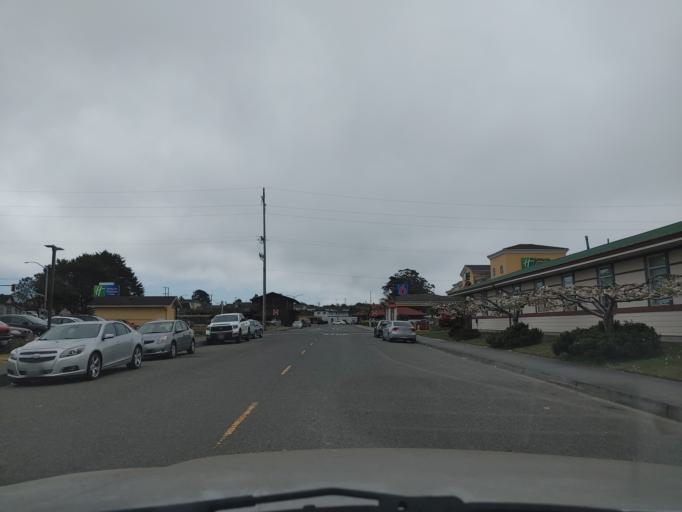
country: US
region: California
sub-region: Humboldt County
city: Eureka
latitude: 40.7921
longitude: -124.1791
